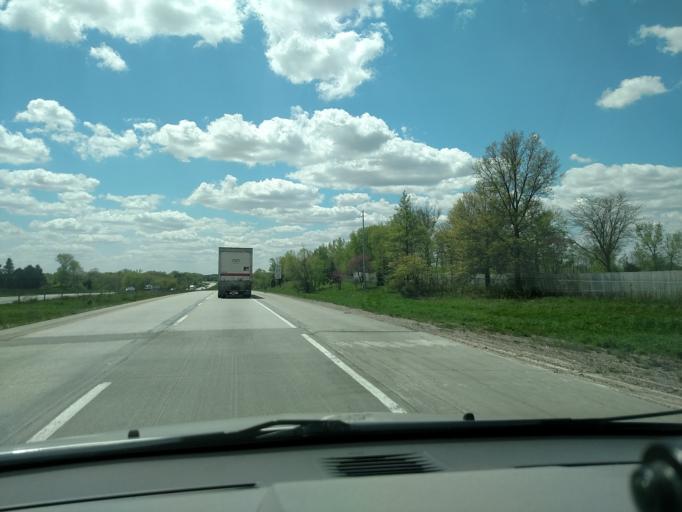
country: US
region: Iowa
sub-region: Polk County
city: Ankeny
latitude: 41.7517
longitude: -93.5733
